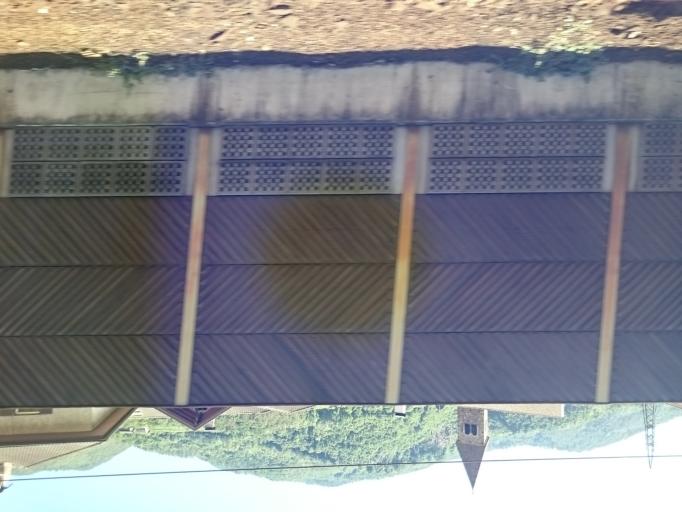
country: IT
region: Trentino-Alto Adige
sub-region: Bolzano
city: Cardano
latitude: 46.4948
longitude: 11.3926
